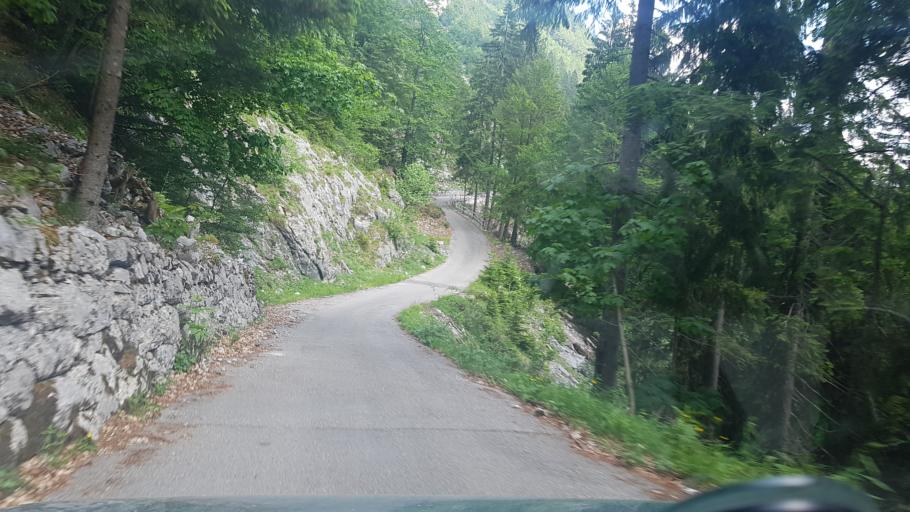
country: IT
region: Friuli Venezia Giulia
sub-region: Provincia di Udine
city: Paularo
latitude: 46.5508
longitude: 13.1996
